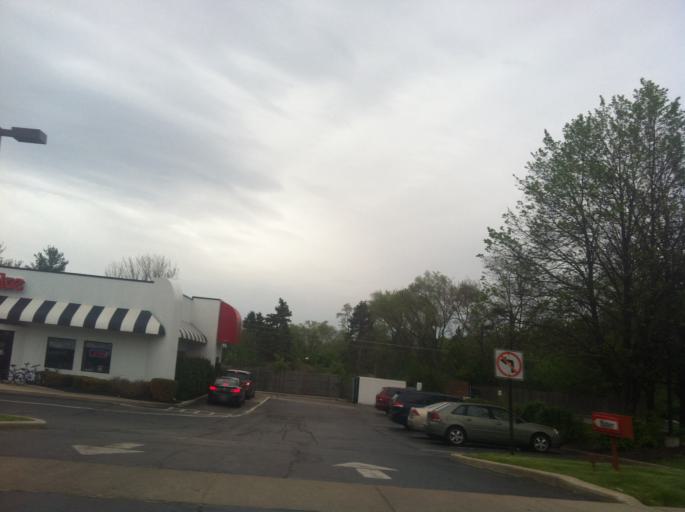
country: US
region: Illinois
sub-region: DuPage County
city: Downers Grove
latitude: 41.8082
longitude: -88.0224
